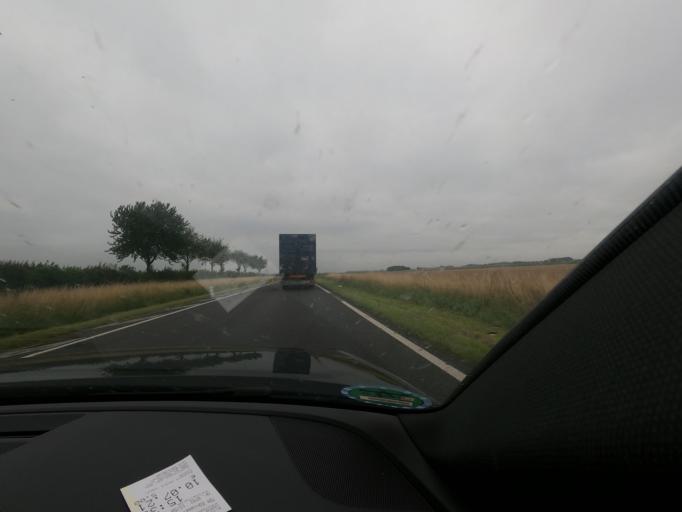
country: FR
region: Picardie
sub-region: Departement de la Somme
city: Harbonnieres
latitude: 49.7814
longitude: 2.5913
